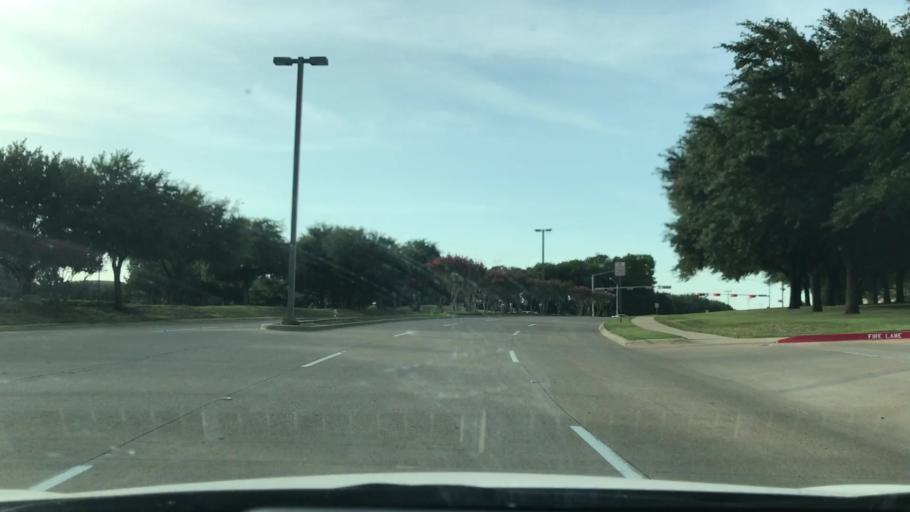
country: US
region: Texas
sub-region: Dallas County
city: Farmers Branch
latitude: 32.8942
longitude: -96.9451
